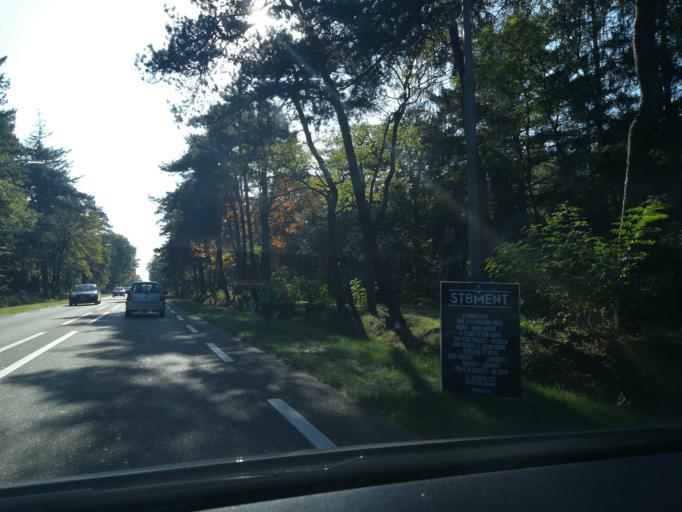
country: NL
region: North Brabant
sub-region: Gemeente Valkenswaard
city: Valkenswaard
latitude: 51.3693
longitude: 5.4661
